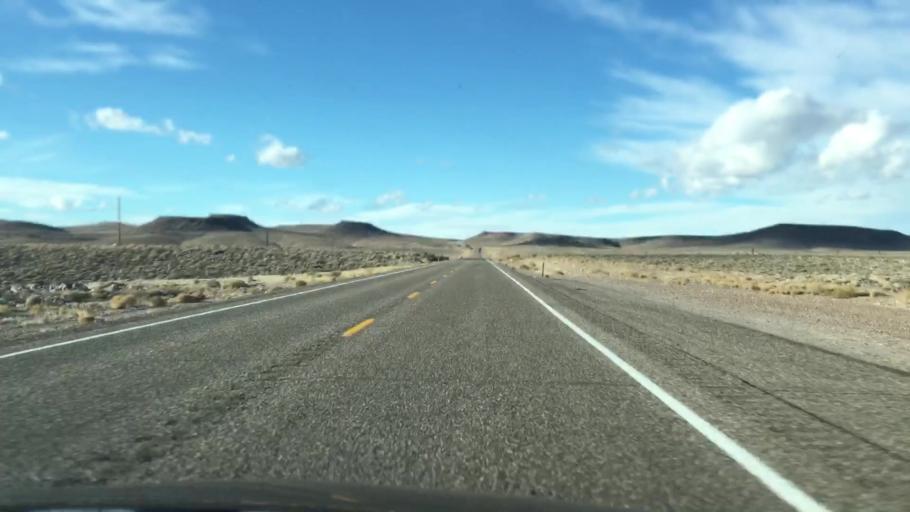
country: US
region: Nevada
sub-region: Esmeralda County
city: Goldfield
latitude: 37.3682
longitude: -117.1237
